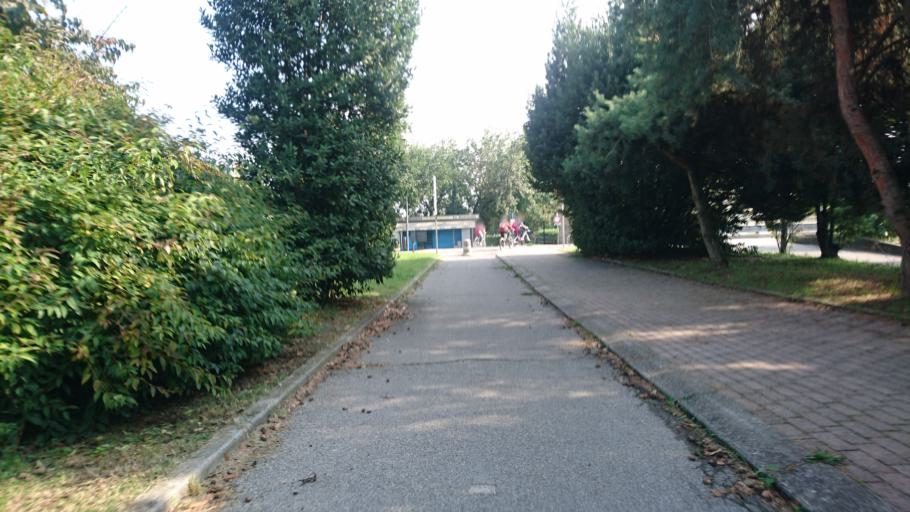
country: IT
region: Veneto
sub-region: Provincia di Rovigo
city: Rovigo
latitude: 45.0658
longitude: 11.7846
